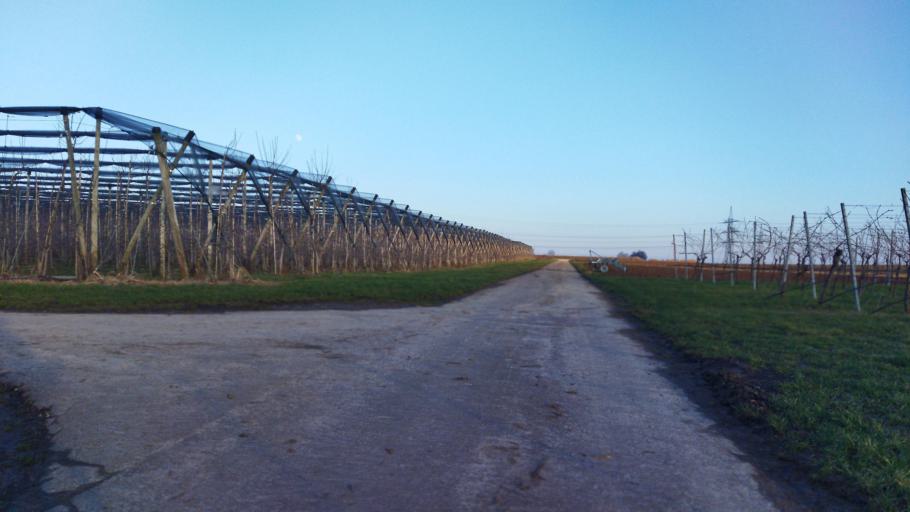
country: DE
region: Baden-Wuerttemberg
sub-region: Regierungsbezirk Stuttgart
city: Neckarwestheim
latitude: 49.0629
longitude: 9.1857
